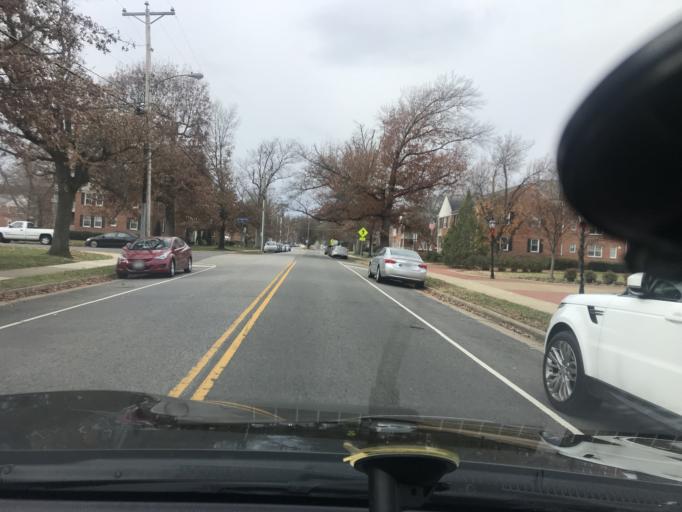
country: US
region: Virginia
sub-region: Fairfax County
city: Belle Haven
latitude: 38.7751
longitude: -77.0553
